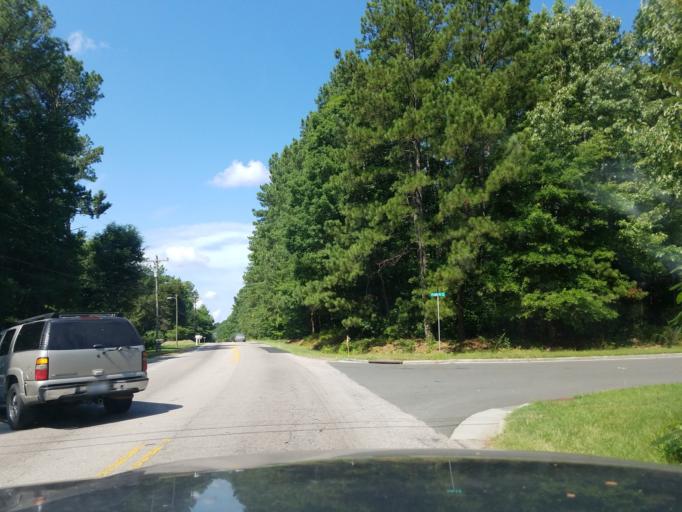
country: US
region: North Carolina
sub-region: Durham County
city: Durham
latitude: 35.9341
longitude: -78.9131
